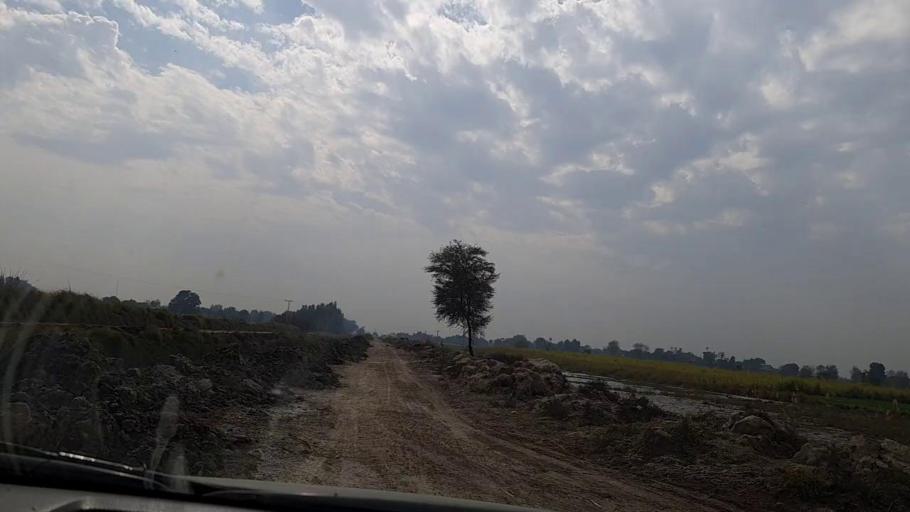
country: PK
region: Sindh
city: Daulatpur
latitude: 26.5646
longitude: 67.9840
